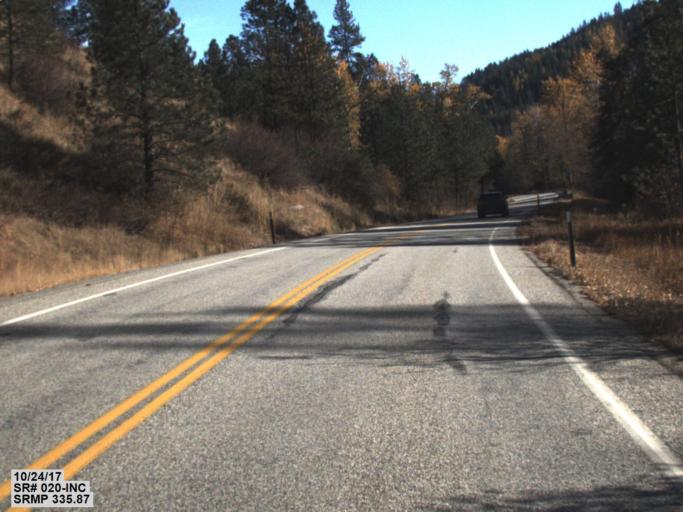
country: US
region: Washington
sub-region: Stevens County
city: Kettle Falls
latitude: 48.5850
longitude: -118.2099
